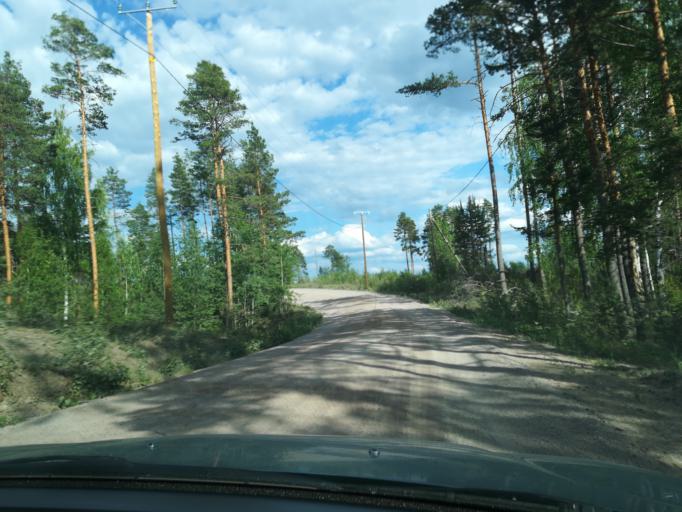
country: FI
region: Southern Savonia
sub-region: Savonlinna
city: Savonlinna
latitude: 61.6330
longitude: 28.7233
